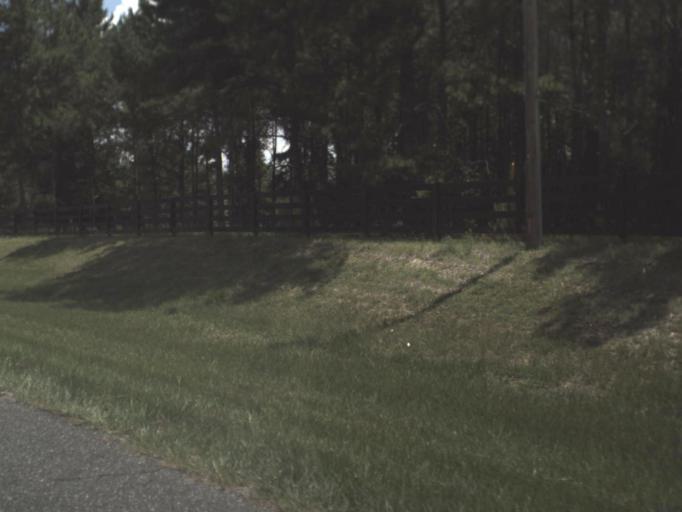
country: US
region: Florida
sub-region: Alachua County
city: High Springs
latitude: 29.8663
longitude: -82.6087
